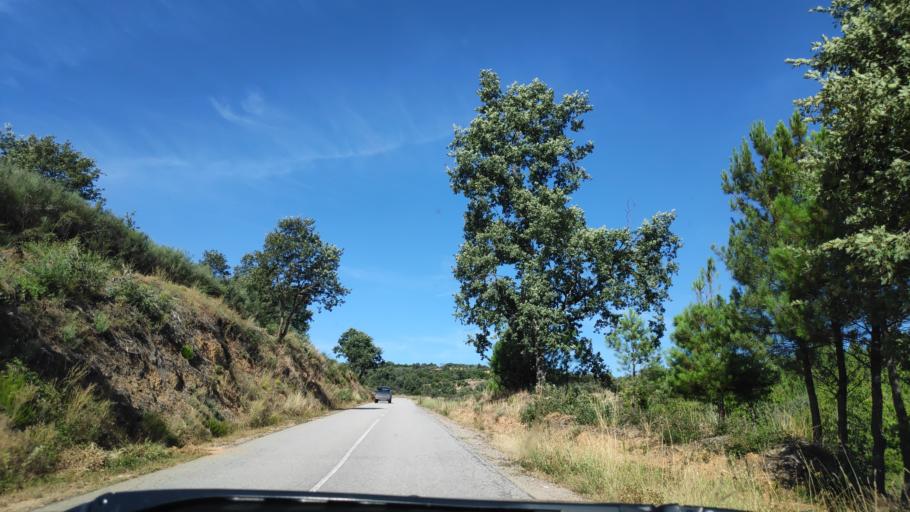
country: ES
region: Castille and Leon
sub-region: Provincia de Zamora
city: Alcanices
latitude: 41.6488
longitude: -6.3670
